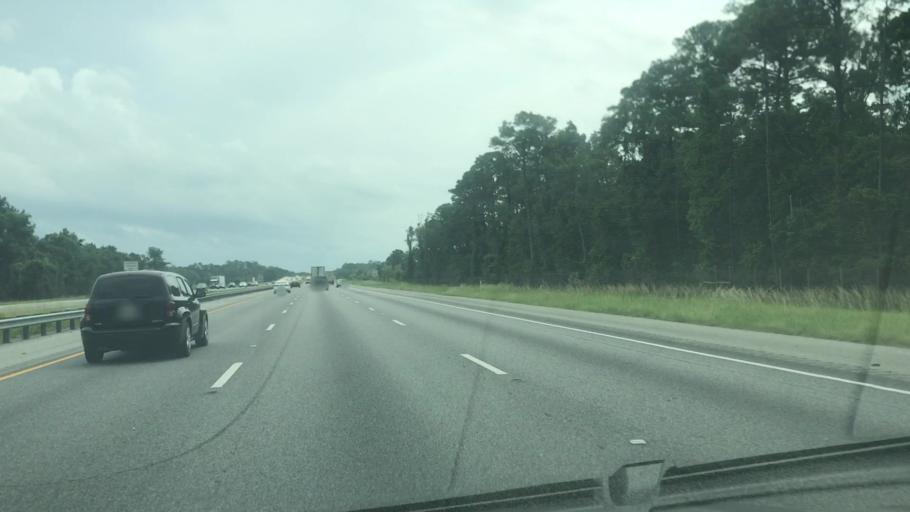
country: US
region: Georgia
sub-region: Glynn County
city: Dock Junction
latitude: 31.1760
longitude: -81.5486
